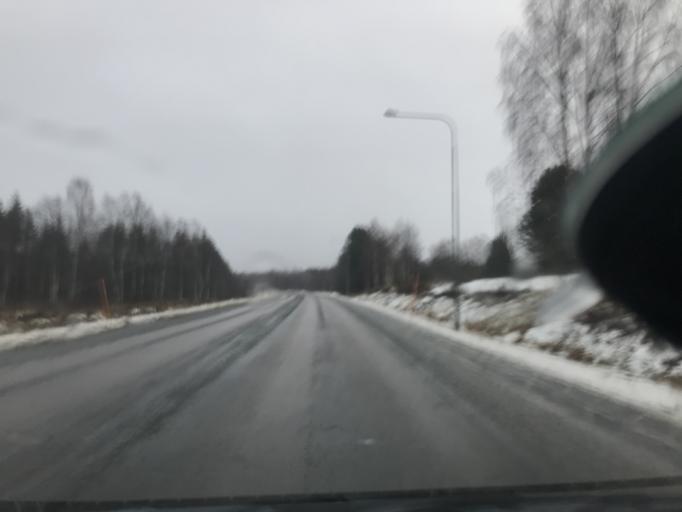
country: SE
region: Norrbotten
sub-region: Lulea Kommun
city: Sodra Sunderbyn
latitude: 65.6565
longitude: 21.9640
